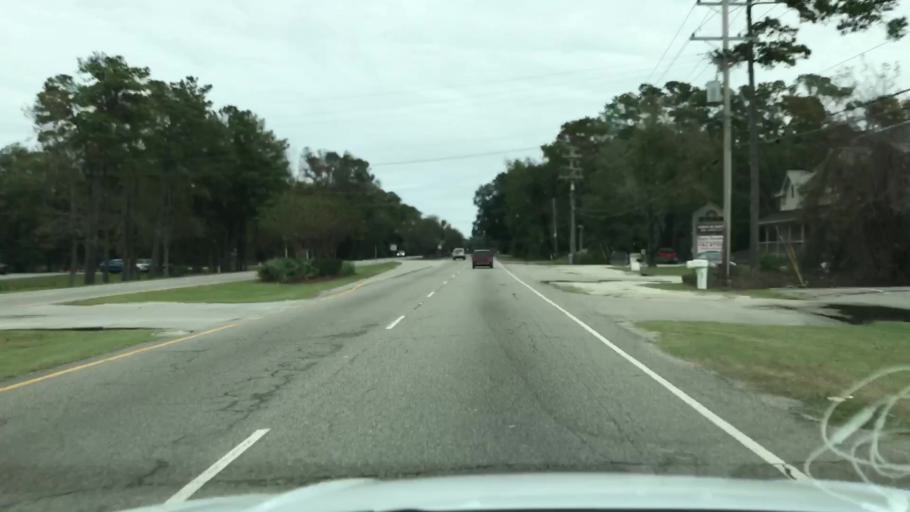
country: US
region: South Carolina
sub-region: Georgetown County
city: Murrells Inlet
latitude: 33.4742
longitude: -79.1032
